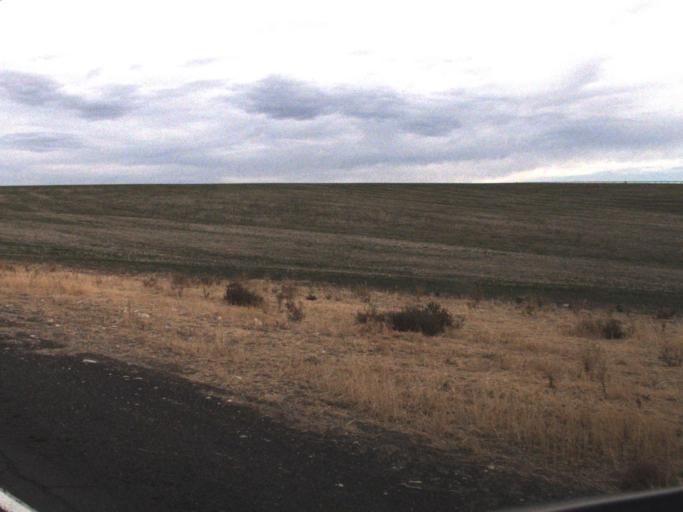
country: US
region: Washington
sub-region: Okanogan County
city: Coulee Dam
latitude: 47.6298
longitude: -118.7207
